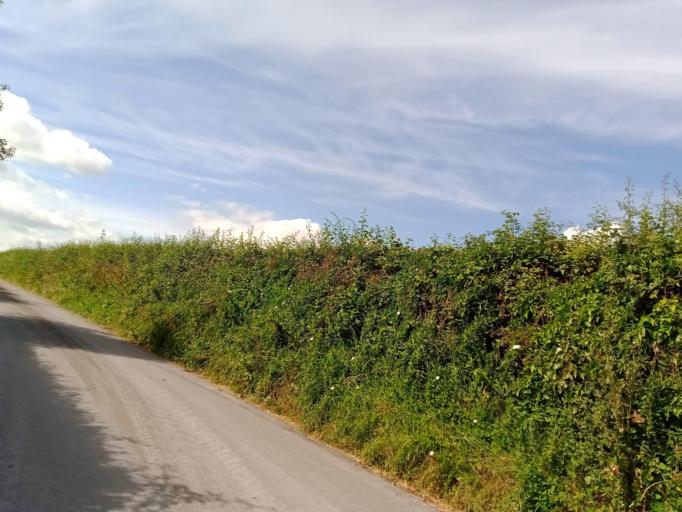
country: IE
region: Leinster
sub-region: Kilkenny
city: Kilkenny
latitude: 52.6352
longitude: -7.2069
